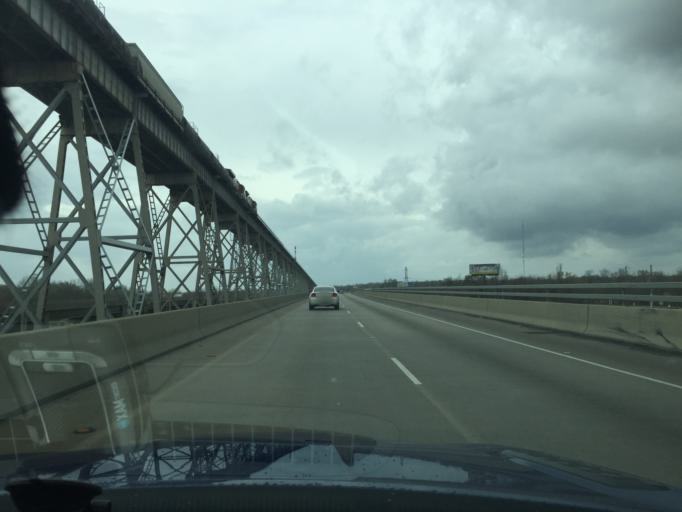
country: US
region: Louisiana
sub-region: Jefferson Parish
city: Bridge City
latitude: 29.9304
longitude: -90.1654
